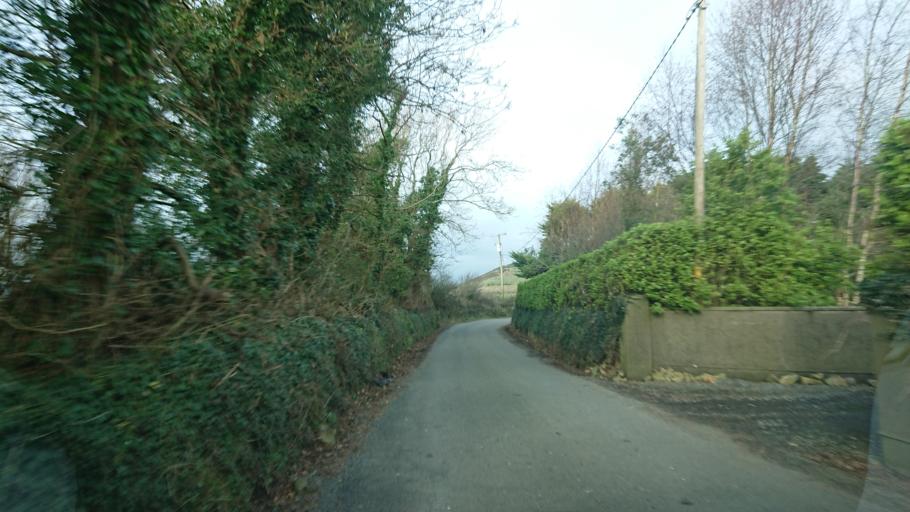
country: IE
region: Munster
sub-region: Waterford
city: Tra Mhor
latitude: 52.1594
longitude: -7.2147
